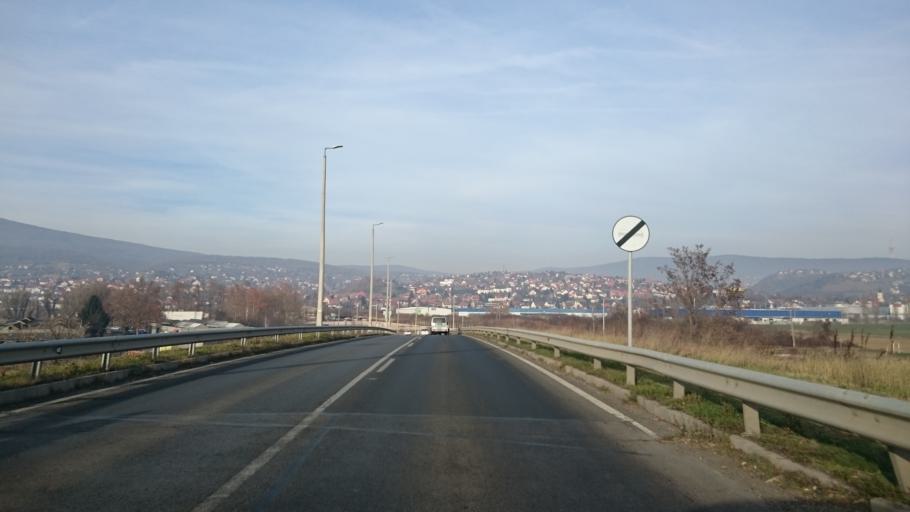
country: HU
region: Baranya
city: Pellerd
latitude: 46.0588
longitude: 18.1755
